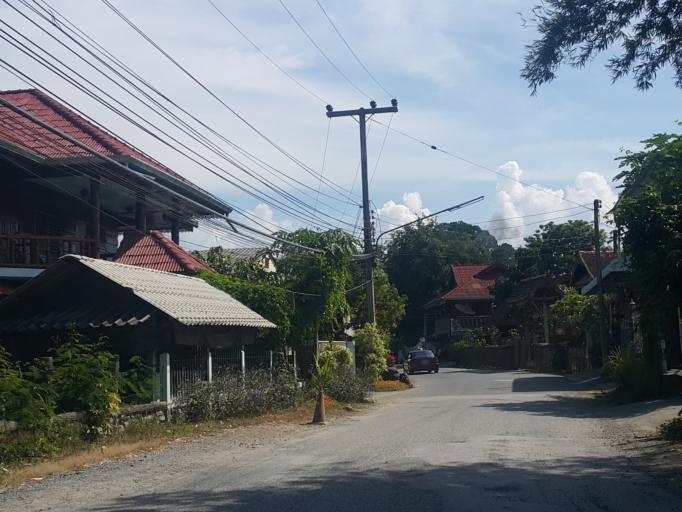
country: TH
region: Chiang Mai
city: San Kamphaeng
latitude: 18.8217
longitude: 99.1689
